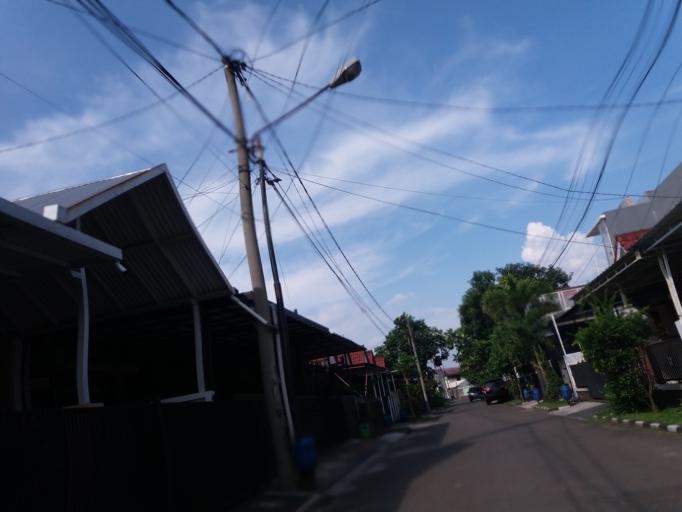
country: ID
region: West Java
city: Bandung
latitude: -6.9301
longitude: 107.6668
